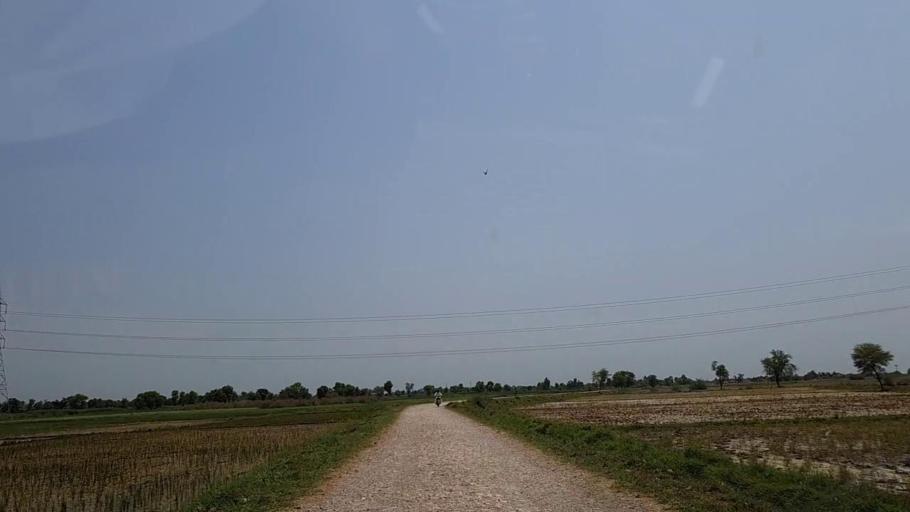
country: PK
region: Sindh
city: Ghotki
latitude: 27.9954
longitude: 69.4106
